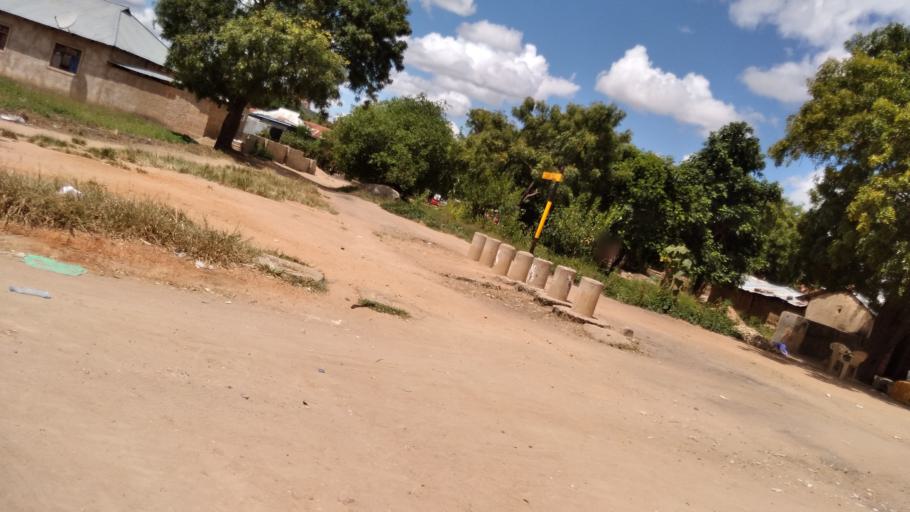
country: TZ
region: Dodoma
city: Dodoma
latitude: -6.1607
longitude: 35.7370
